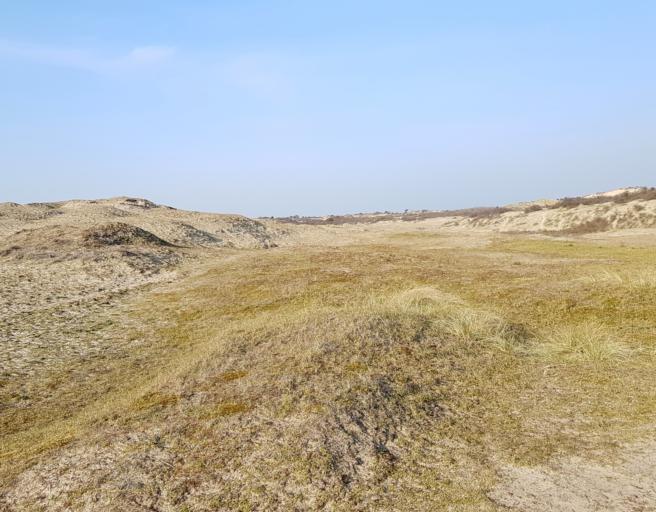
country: NL
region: South Holland
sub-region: Gemeente Noordwijkerhout
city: Noordwijkerhout
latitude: 52.2991
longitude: 4.4852
